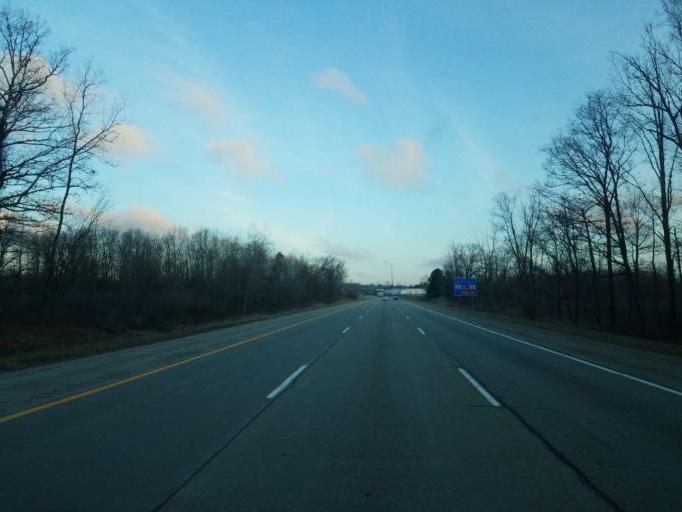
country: US
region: Michigan
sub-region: Livingston County
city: Brighton
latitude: 42.5746
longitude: -83.8492
